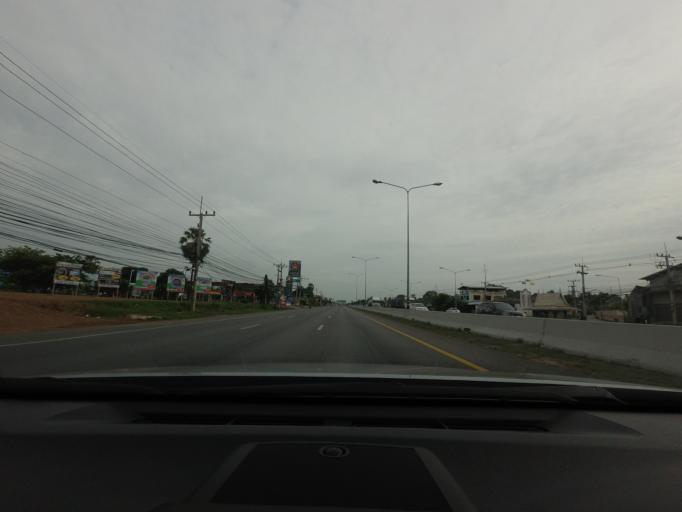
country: TH
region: Phetchaburi
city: Ban Lat
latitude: 13.0689
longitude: 99.9467
